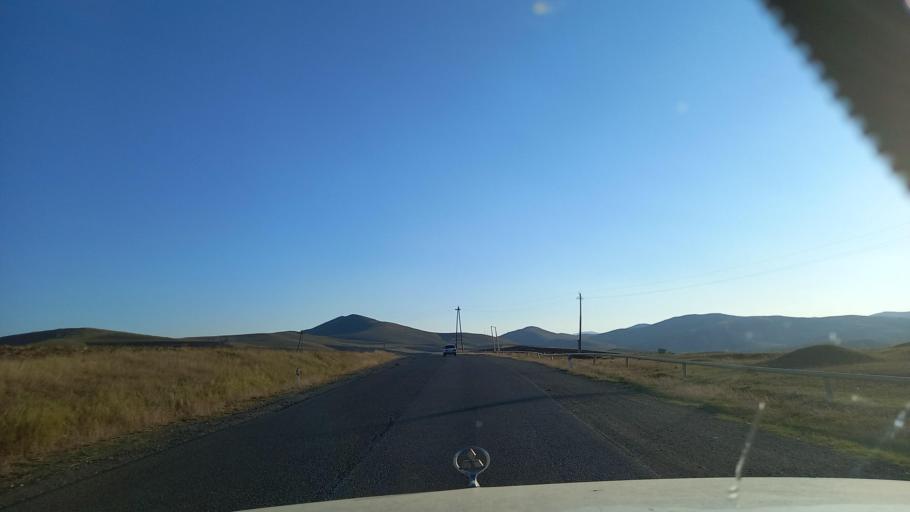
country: AZ
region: Shamkir Rayon
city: Shamkhor
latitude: 40.7577
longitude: 45.9066
